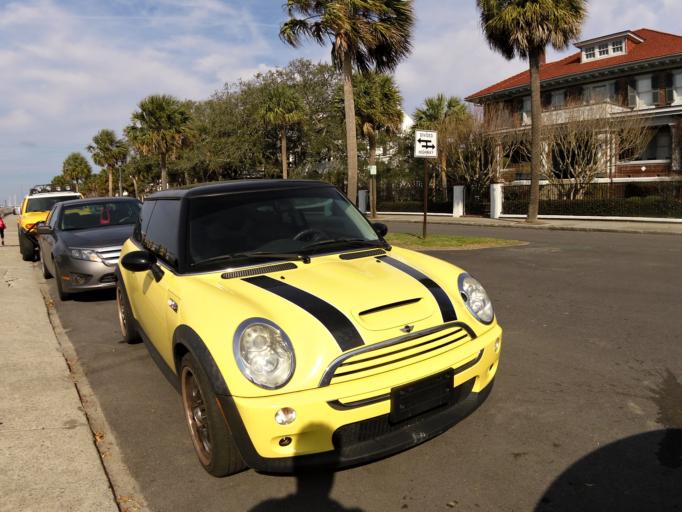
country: US
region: South Carolina
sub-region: Charleston County
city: Charleston
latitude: 32.7713
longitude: -79.9401
